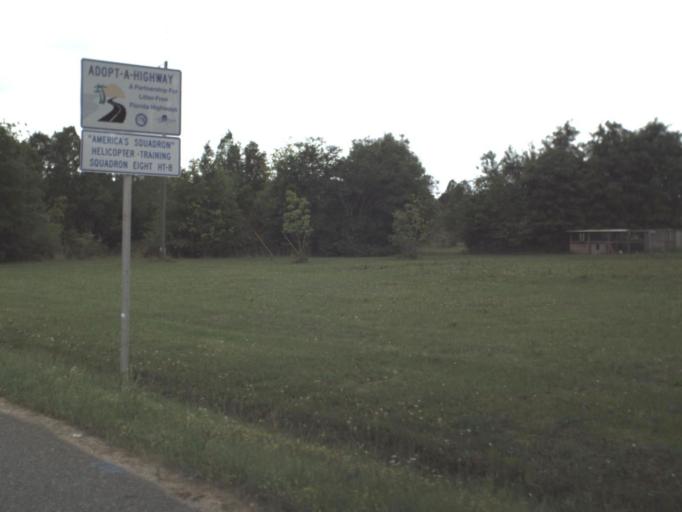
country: US
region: Florida
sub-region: Santa Rosa County
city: Point Baker
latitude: 30.7617
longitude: -87.0423
